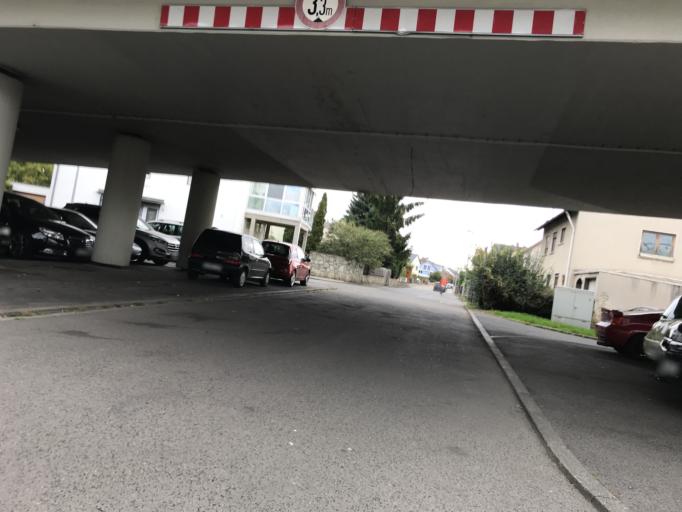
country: DE
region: Rheinland-Pfalz
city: Mainz
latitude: 50.0051
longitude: 8.3014
